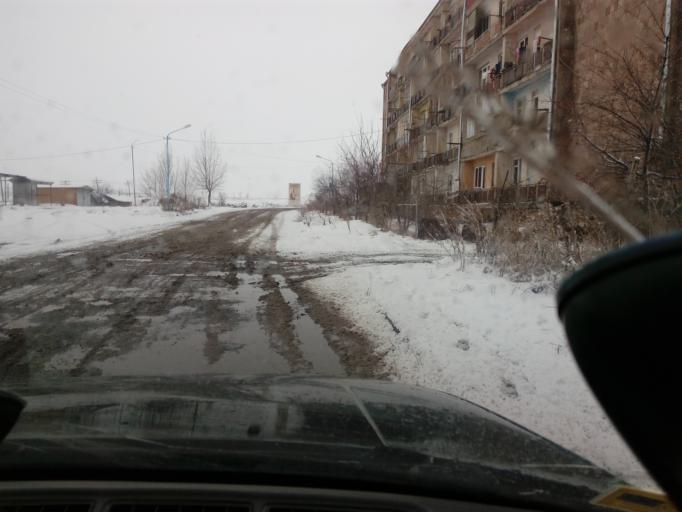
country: AM
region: Geghark'unik'i Marz
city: Gagarin
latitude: 40.5357
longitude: 44.8768
